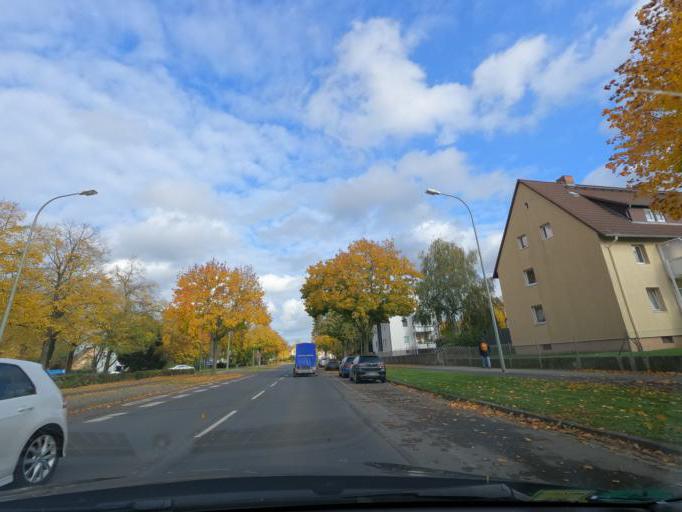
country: DE
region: Lower Saxony
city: Wolfenbuettel
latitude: 52.1594
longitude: 10.5123
